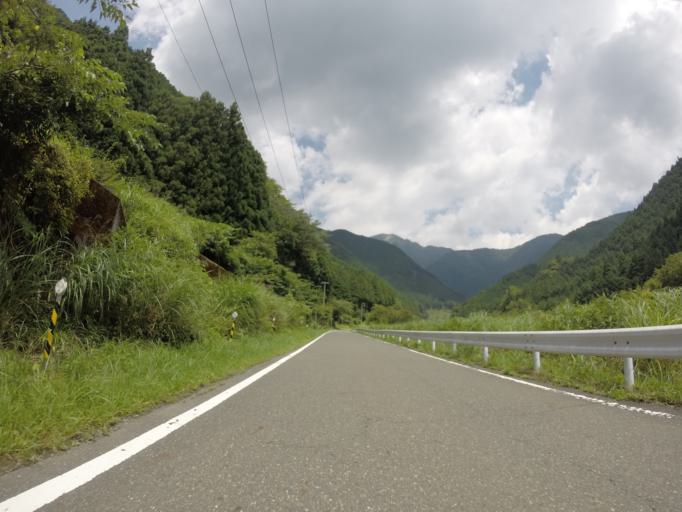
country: JP
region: Shizuoka
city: Fujinomiya
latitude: 35.2921
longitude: 138.3360
